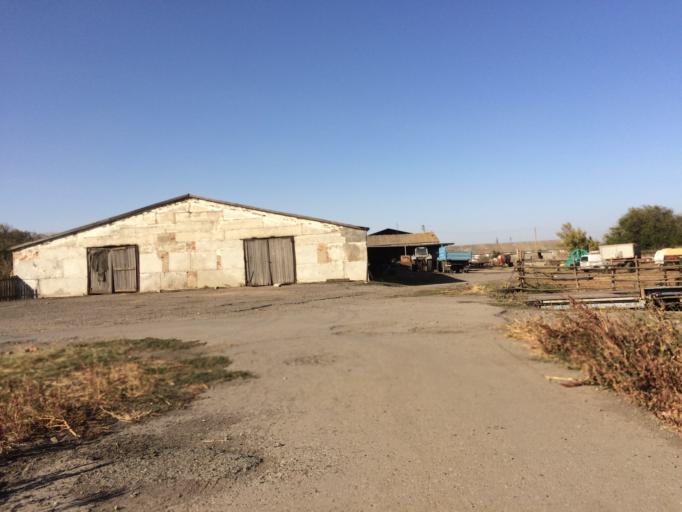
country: RU
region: Rostov
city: Gigant
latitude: 46.5193
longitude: 41.1948
